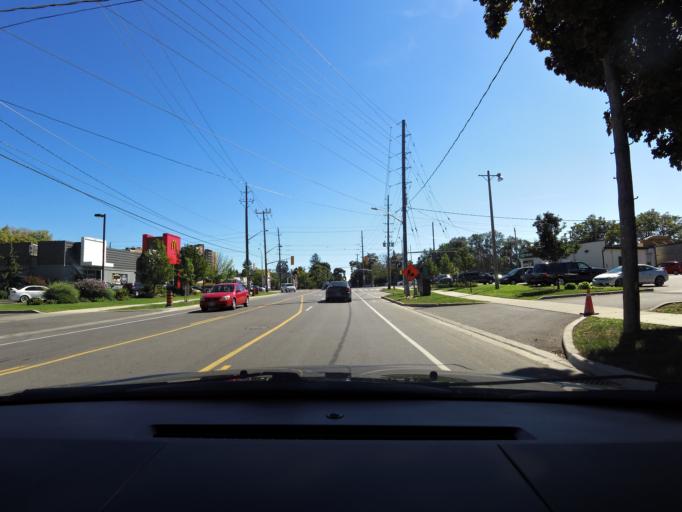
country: CA
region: Ontario
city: Burlington
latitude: 43.3224
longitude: -79.8334
